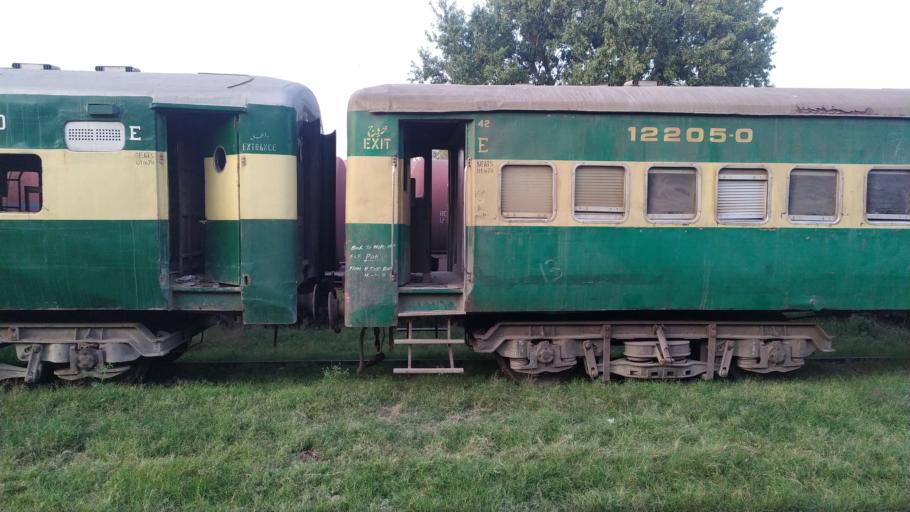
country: PK
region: Punjab
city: Rawalpindi
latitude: 33.6041
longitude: 73.0492
